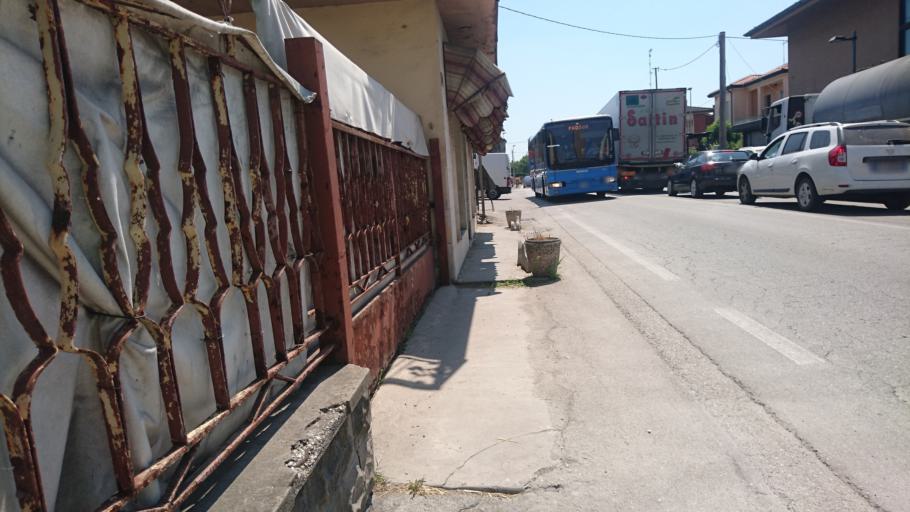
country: IT
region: Veneto
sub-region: Provincia di Padova
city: Solesino
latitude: 45.1773
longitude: 11.7434
